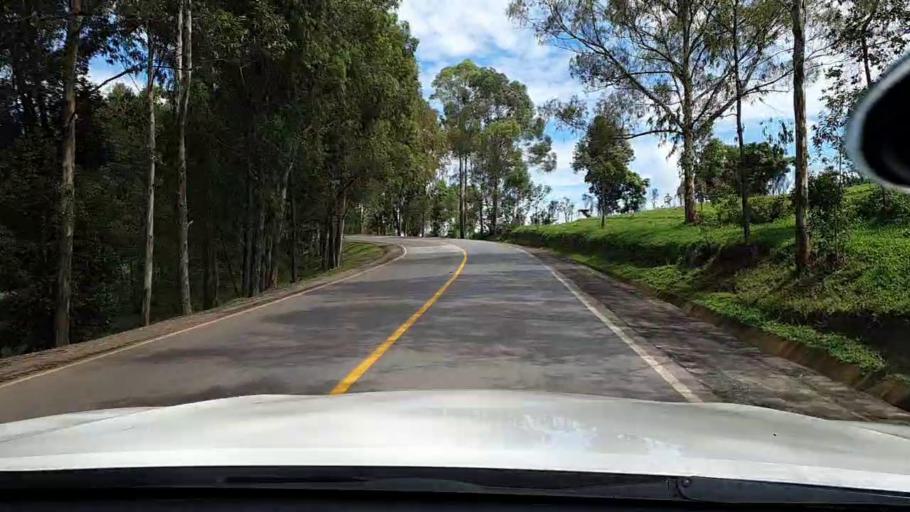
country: RW
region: Kigali
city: Kigali
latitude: -1.8178
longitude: 29.9412
